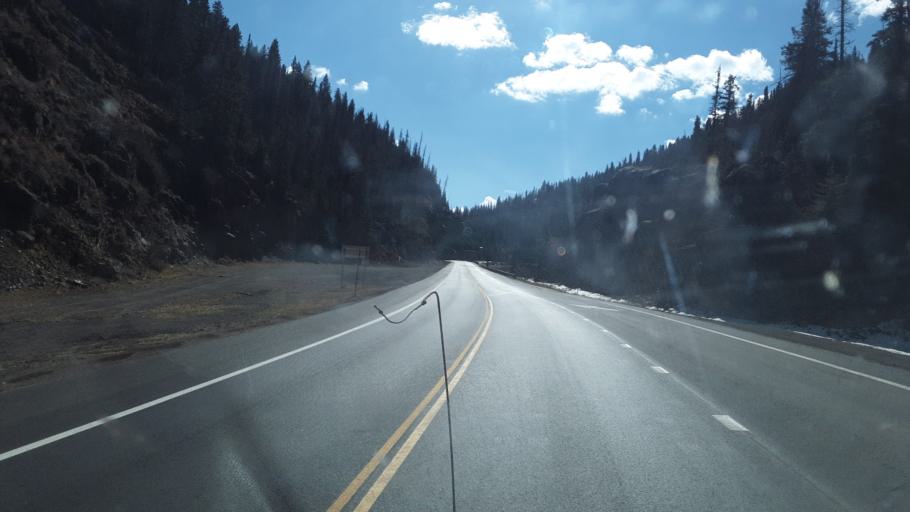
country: US
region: Colorado
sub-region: Mineral County
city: Creede
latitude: 37.5531
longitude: -106.7767
